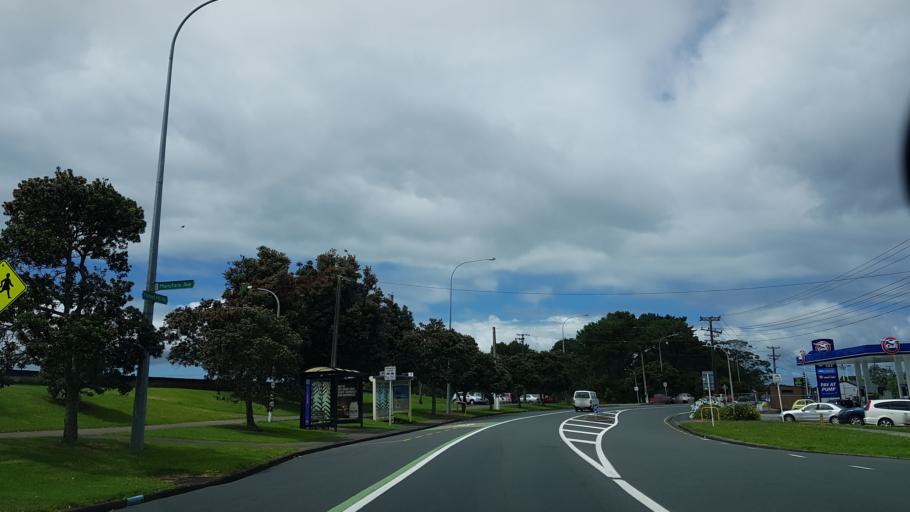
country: NZ
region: Auckland
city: Murrays Bay
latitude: -36.7574
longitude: 174.7510
